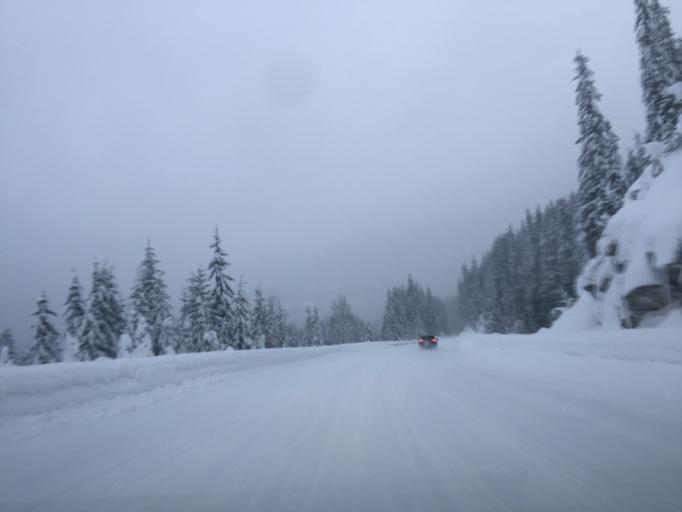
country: US
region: Washington
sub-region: Chelan County
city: Leavenworth
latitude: 47.7826
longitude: -121.0277
